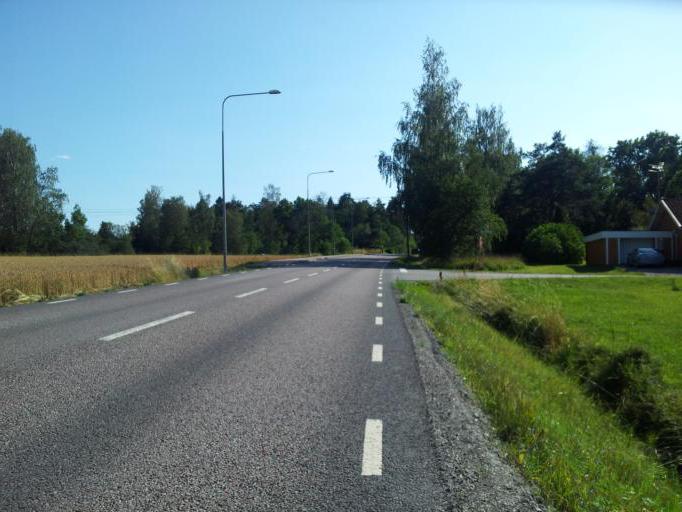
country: SE
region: Uppsala
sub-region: Knivsta Kommun
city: Knivsta
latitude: 59.8798
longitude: 17.9688
